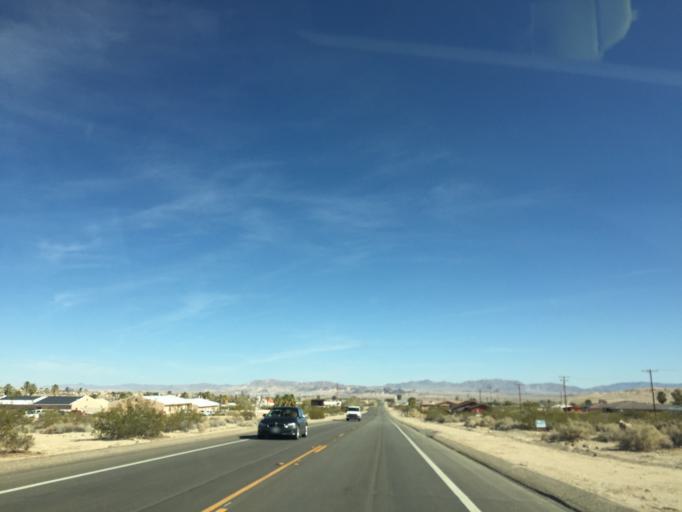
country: US
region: California
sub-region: San Bernardino County
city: Twentynine Palms
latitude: 34.1254
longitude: -116.0367
